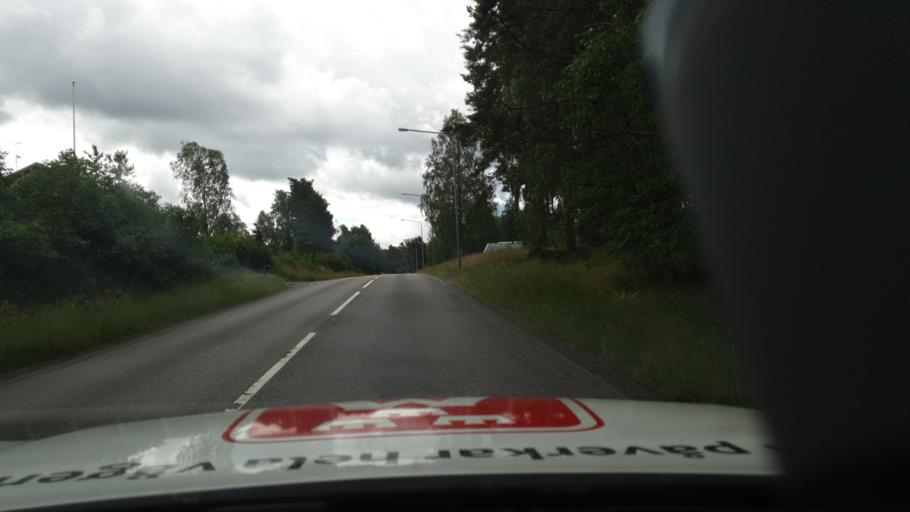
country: SE
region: Joenkoeping
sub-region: Mullsjo Kommun
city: Mullsjoe
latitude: 57.9253
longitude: 13.8578
